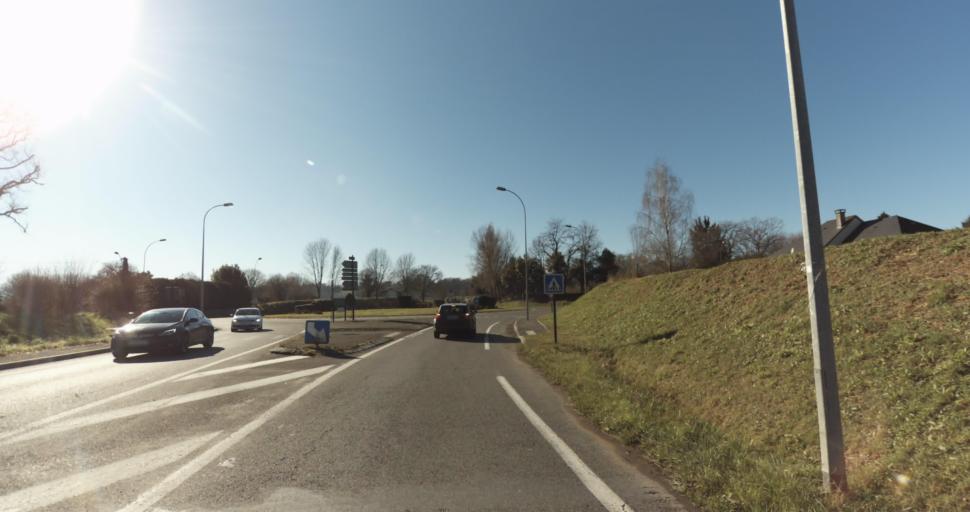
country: FR
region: Aquitaine
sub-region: Departement des Pyrenees-Atlantiques
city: Morlaas
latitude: 43.3392
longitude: -0.2514
